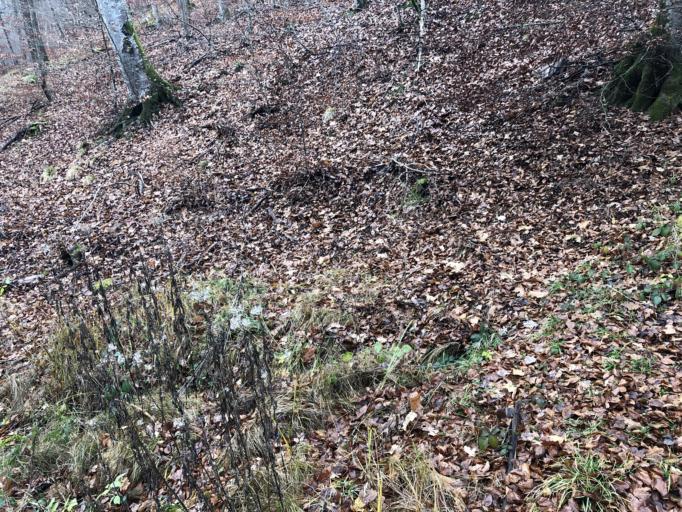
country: DE
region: Baden-Wuerttemberg
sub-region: Tuebingen Region
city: Tuebingen
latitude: 48.5626
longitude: 9.0179
